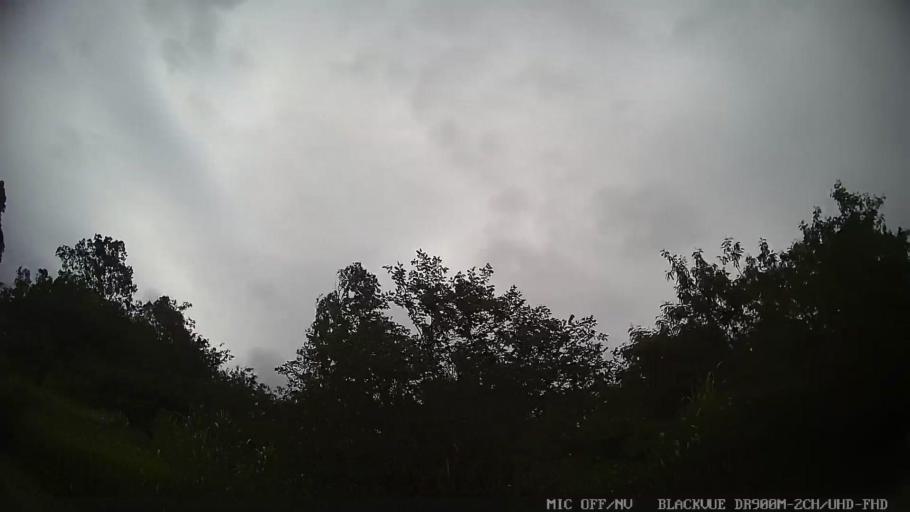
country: BR
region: Sao Paulo
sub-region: Osasco
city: Osasco
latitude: -23.4760
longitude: -46.7325
